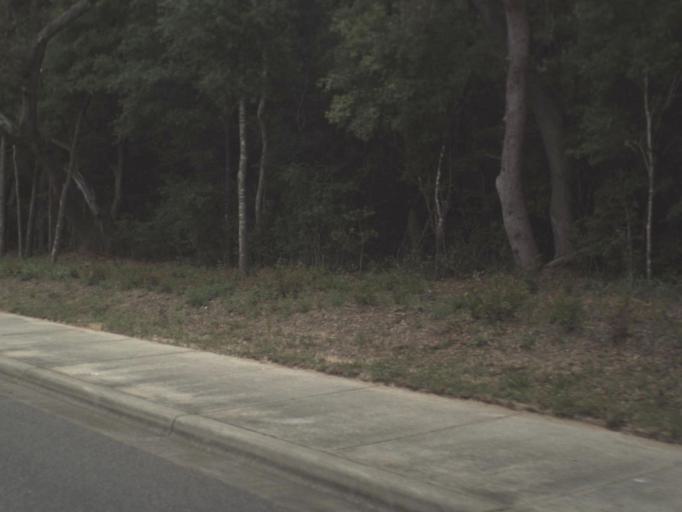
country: US
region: Florida
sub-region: Santa Rosa County
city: Point Baker
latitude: 30.6731
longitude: -87.0543
